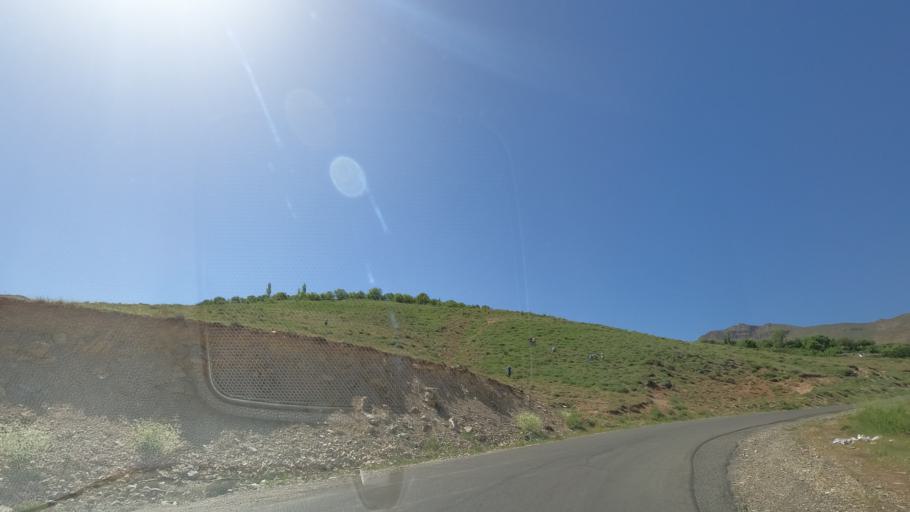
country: IR
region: Alborz
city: Karaj
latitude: 35.9247
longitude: 51.1578
